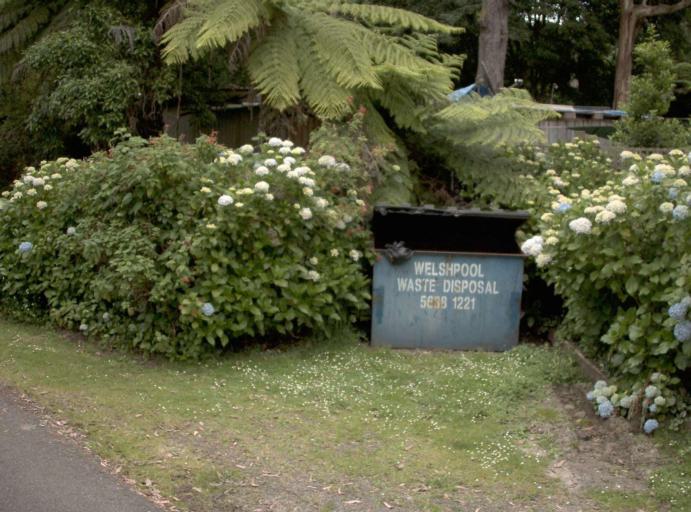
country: AU
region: Victoria
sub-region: Latrobe
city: Traralgon
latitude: -38.4709
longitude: 146.5635
